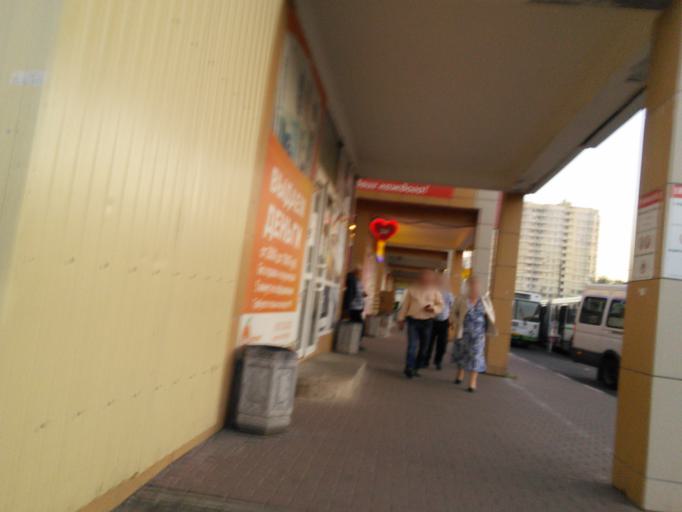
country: RU
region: Moskovskaya
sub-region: Podol'skiy Rayon
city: Podol'sk
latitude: 55.4321
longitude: 37.5642
